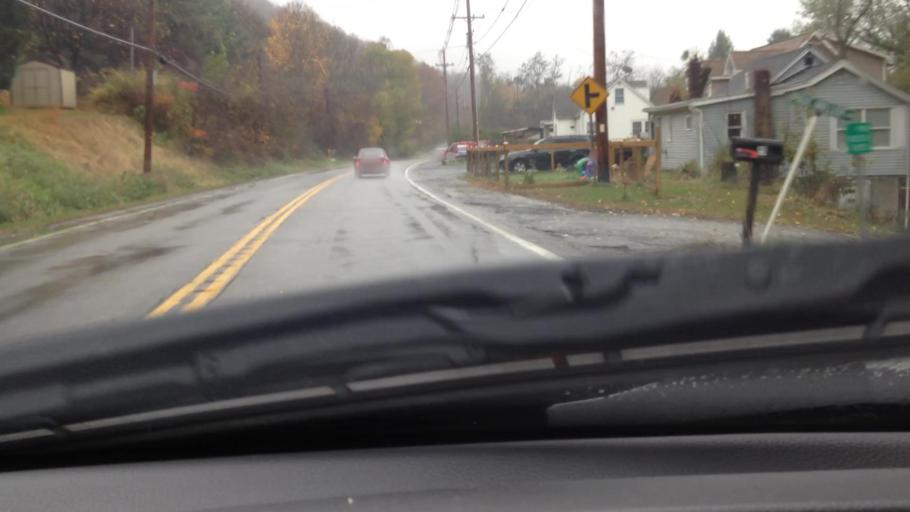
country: US
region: New York
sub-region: Dutchess County
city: Beacon
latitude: 41.4770
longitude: -73.9732
